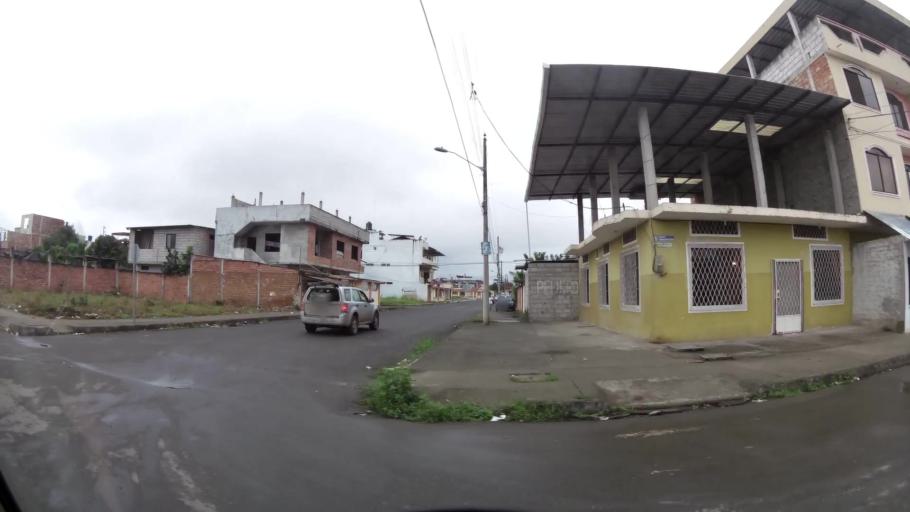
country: EC
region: El Oro
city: Pasaje
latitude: -3.3242
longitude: -79.8154
